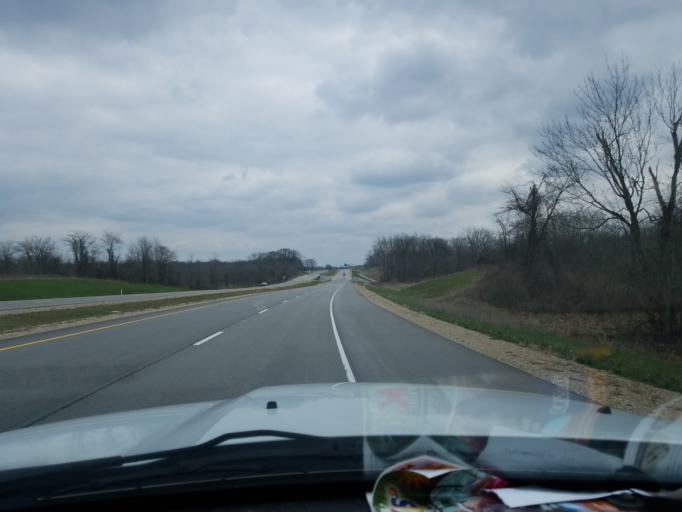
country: US
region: Indiana
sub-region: Vigo County
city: Terre Haute
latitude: 39.4130
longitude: -87.3527
